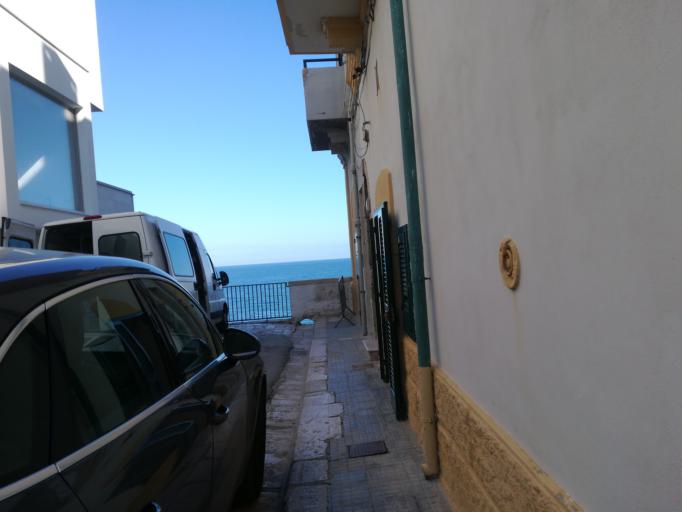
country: IT
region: Apulia
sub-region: Provincia di Bari
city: Polignano a Mare
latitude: 40.9959
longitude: 17.2213
